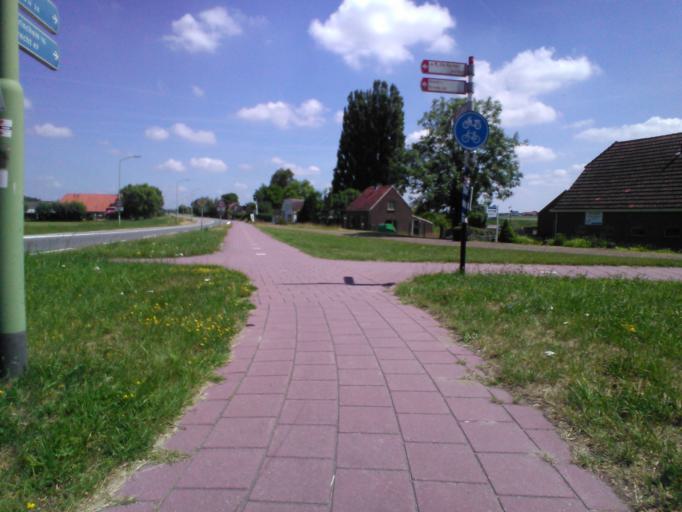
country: NL
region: North Brabant
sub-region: Gemeente Geertruidenberg
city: Geertruidenberg
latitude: 51.7252
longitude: 4.8991
